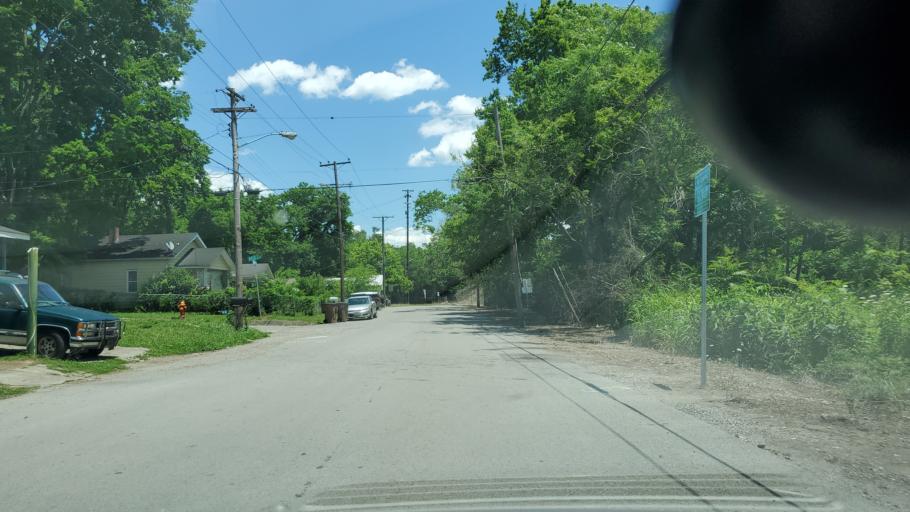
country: US
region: Tennessee
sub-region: Davidson County
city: Nashville
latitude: 36.1890
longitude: -86.7565
